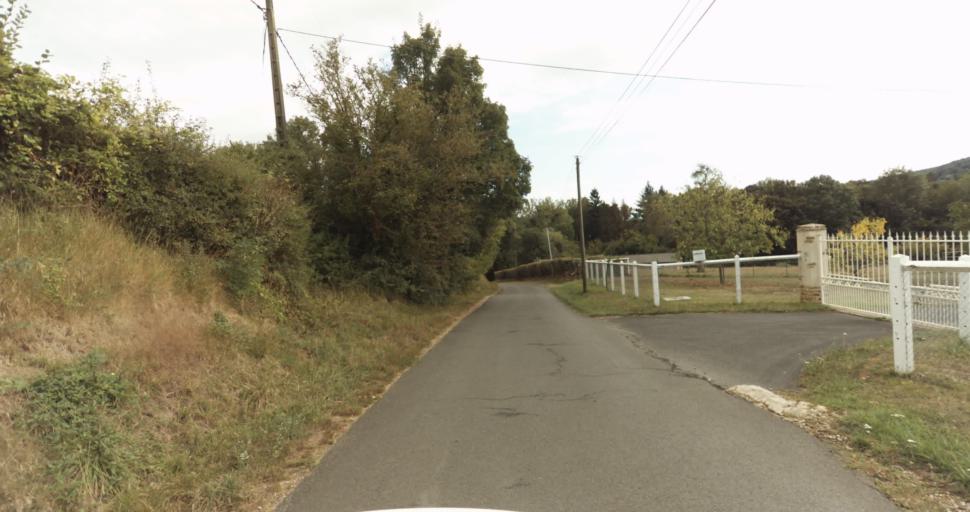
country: FR
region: Lower Normandy
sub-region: Departement de l'Orne
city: Vimoutiers
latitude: 48.9143
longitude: 0.2108
